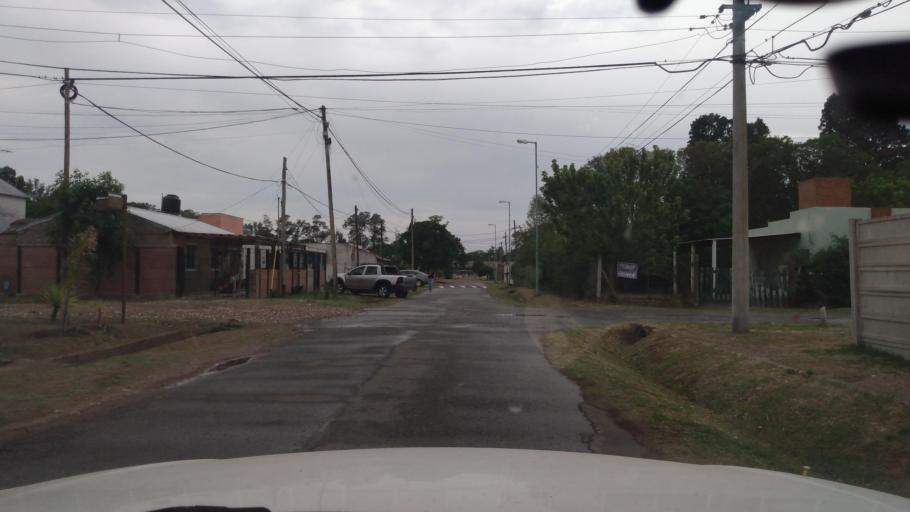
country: AR
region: Buenos Aires
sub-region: Partido de Lujan
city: Lujan
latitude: -34.5549
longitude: -59.2026
